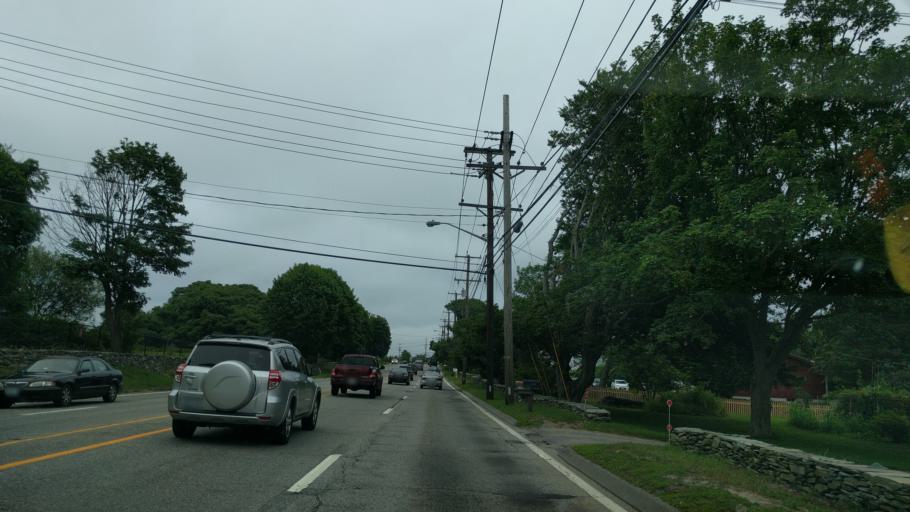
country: US
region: Rhode Island
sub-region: Newport County
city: Melville
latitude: 41.5721
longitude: -71.2748
